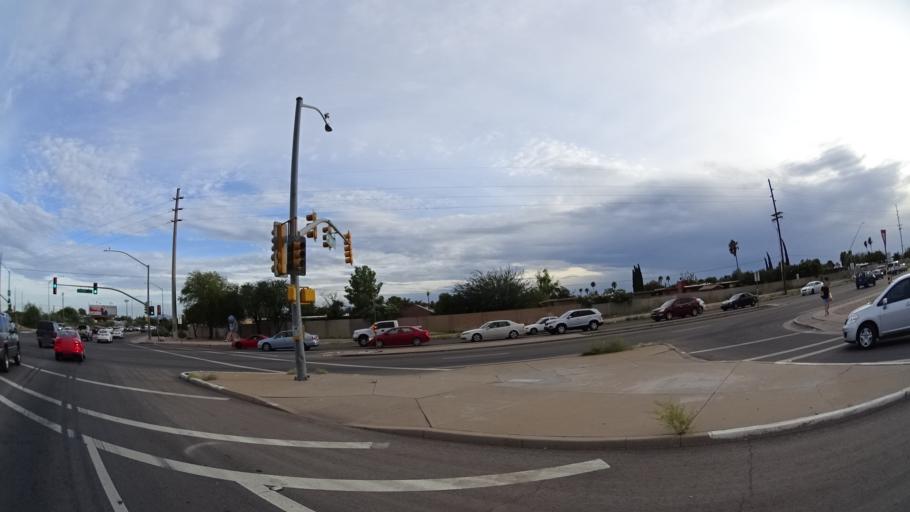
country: US
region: Arizona
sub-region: Pima County
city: South Tucson
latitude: 32.1635
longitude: -110.9360
